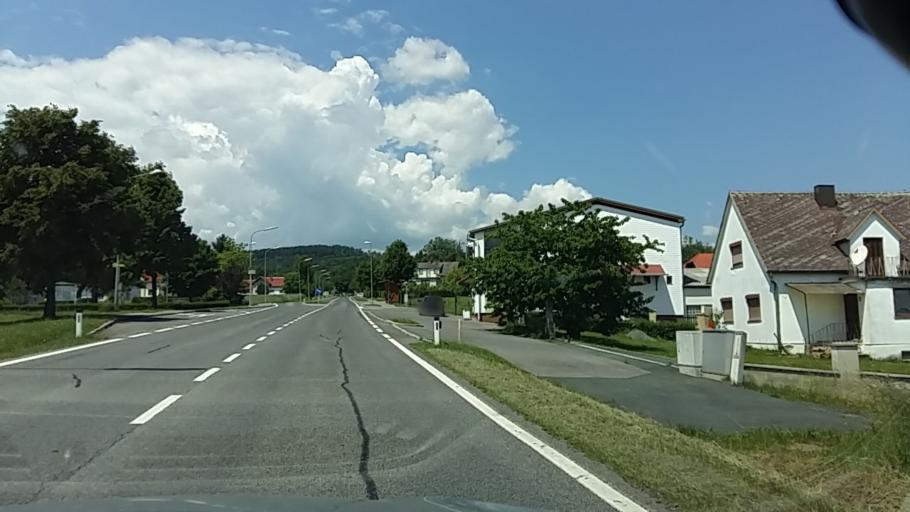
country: AT
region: Burgenland
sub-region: Politischer Bezirk Oberwart
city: Unterkohlstatten
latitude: 47.3961
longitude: 16.3222
